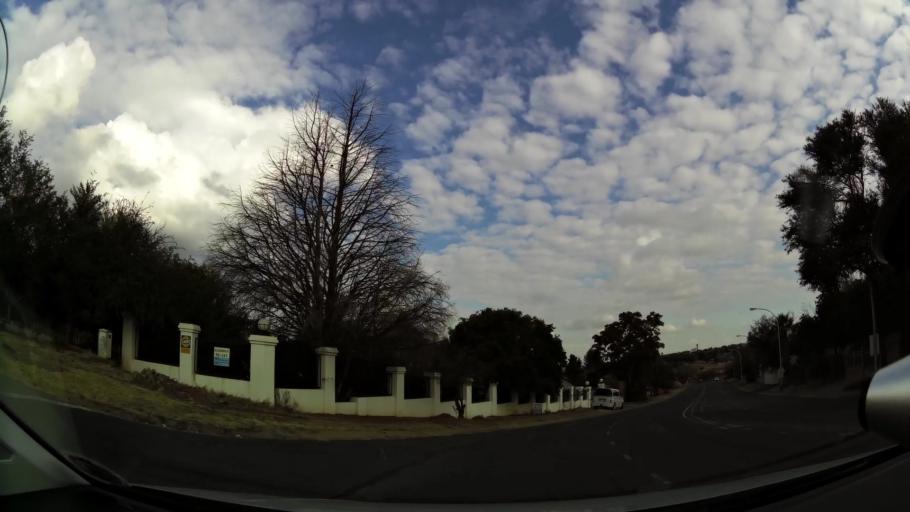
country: ZA
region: Orange Free State
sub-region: Mangaung Metropolitan Municipality
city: Bloemfontein
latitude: -29.0833
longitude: 26.2036
